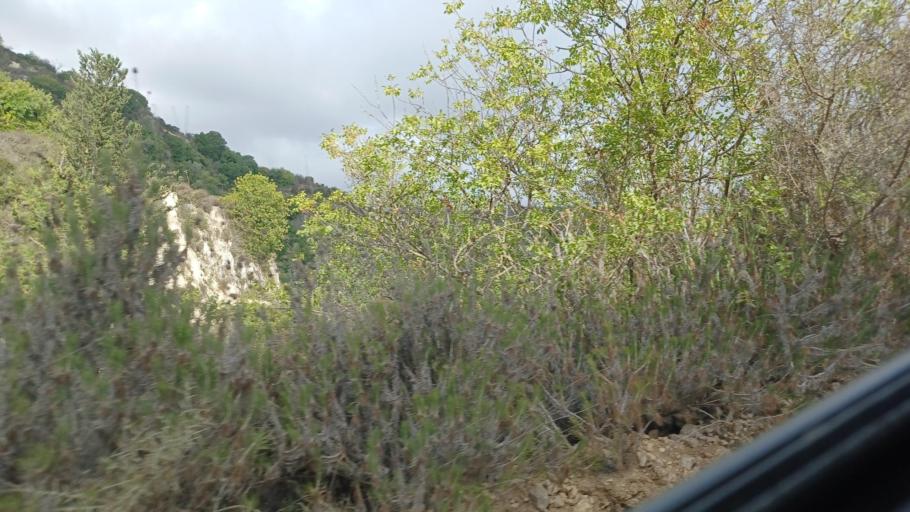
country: CY
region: Pafos
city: Tala
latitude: 34.8725
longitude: 32.4581
